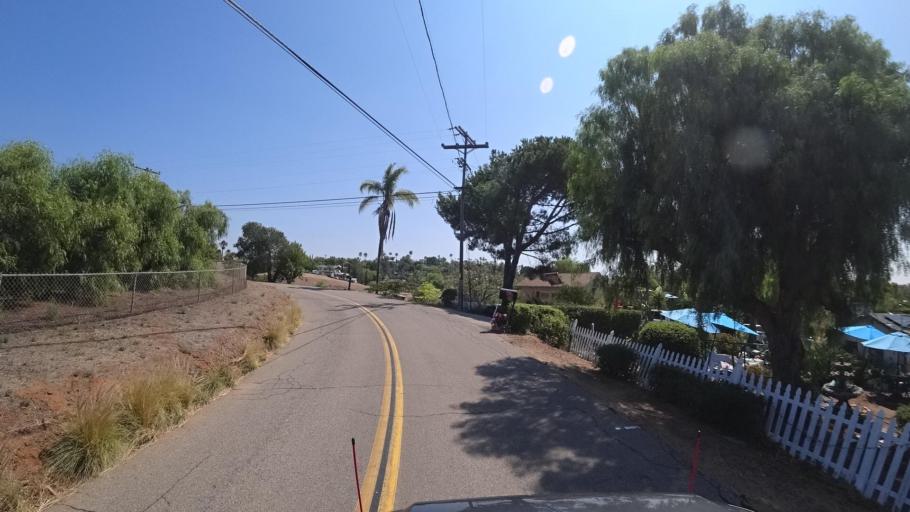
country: US
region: California
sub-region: San Diego County
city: Vista
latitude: 33.2424
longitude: -117.2368
